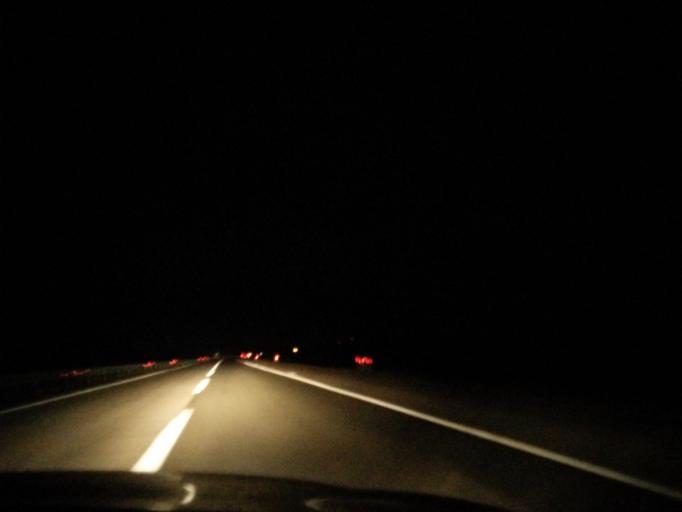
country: RS
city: Visnjicevo
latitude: 45.0376
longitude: 19.2957
